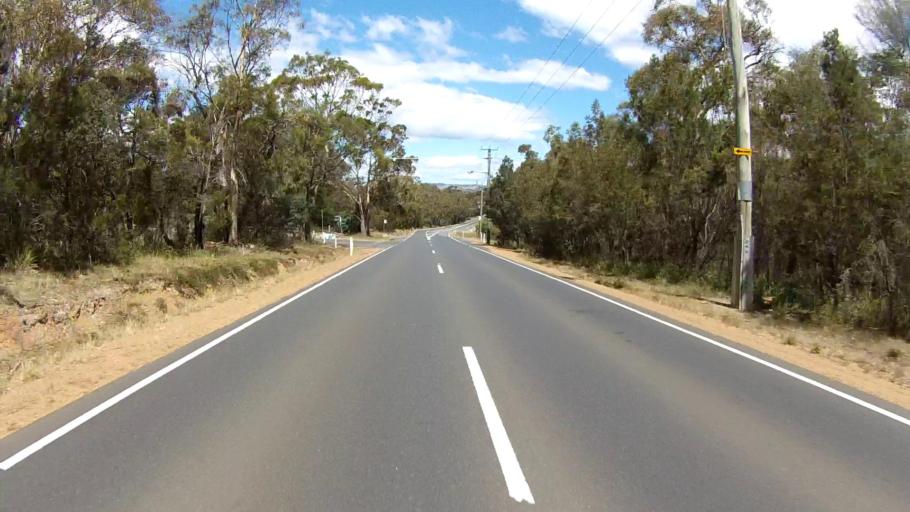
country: AU
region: Tasmania
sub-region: Clarence
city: Acton Park
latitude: -42.8832
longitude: 147.4827
